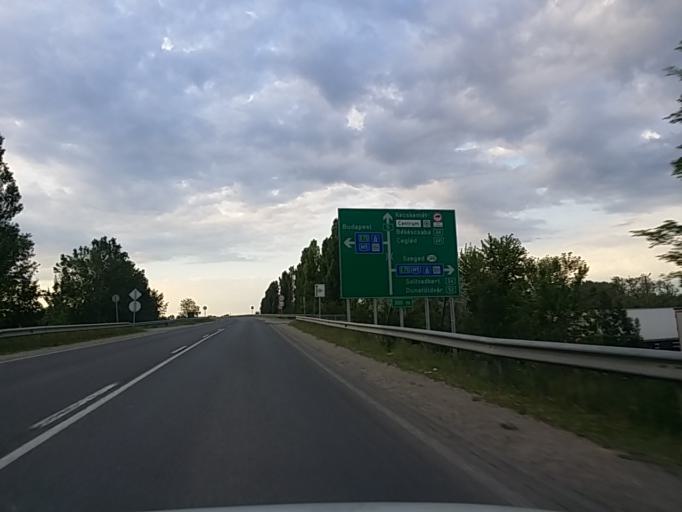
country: HU
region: Bacs-Kiskun
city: Lajosmizse
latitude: 46.9931
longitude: 19.6055
